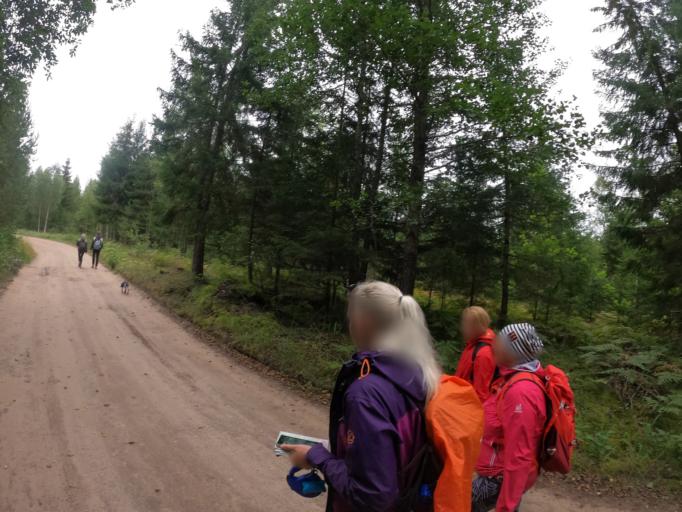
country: LV
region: Kuldigas Rajons
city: Kuldiga
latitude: 57.0175
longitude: 21.9958
